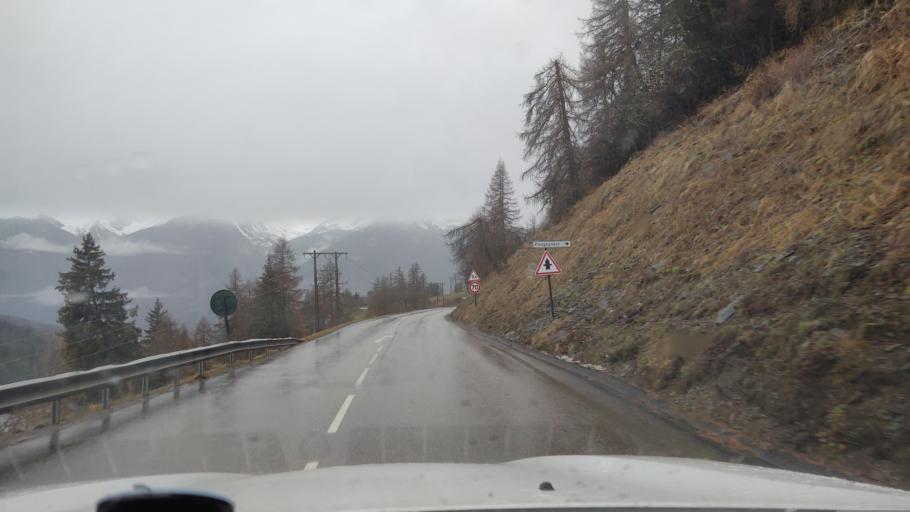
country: FR
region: Rhone-Alpes
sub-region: Departement de la Savoie
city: Macot-la-Plagne
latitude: 45.5247
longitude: 6.6780
